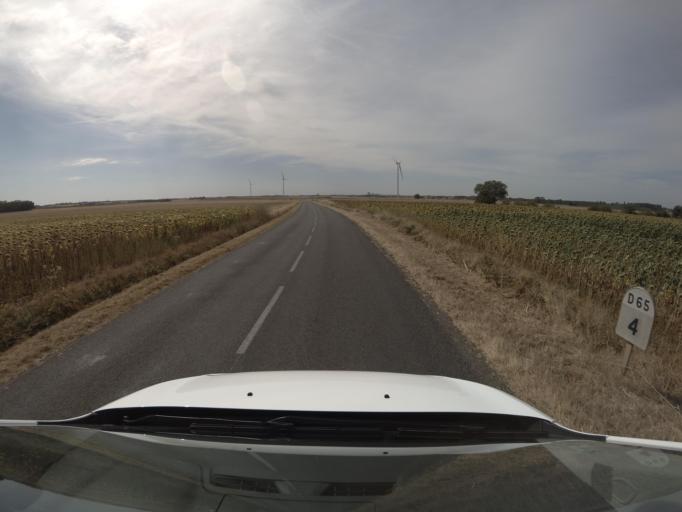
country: FR
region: Poitou-Charentes
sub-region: Departement des Deux-Sevres
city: Saint-Leger-de-Montbrun
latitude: 46.9896
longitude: -0.1493
